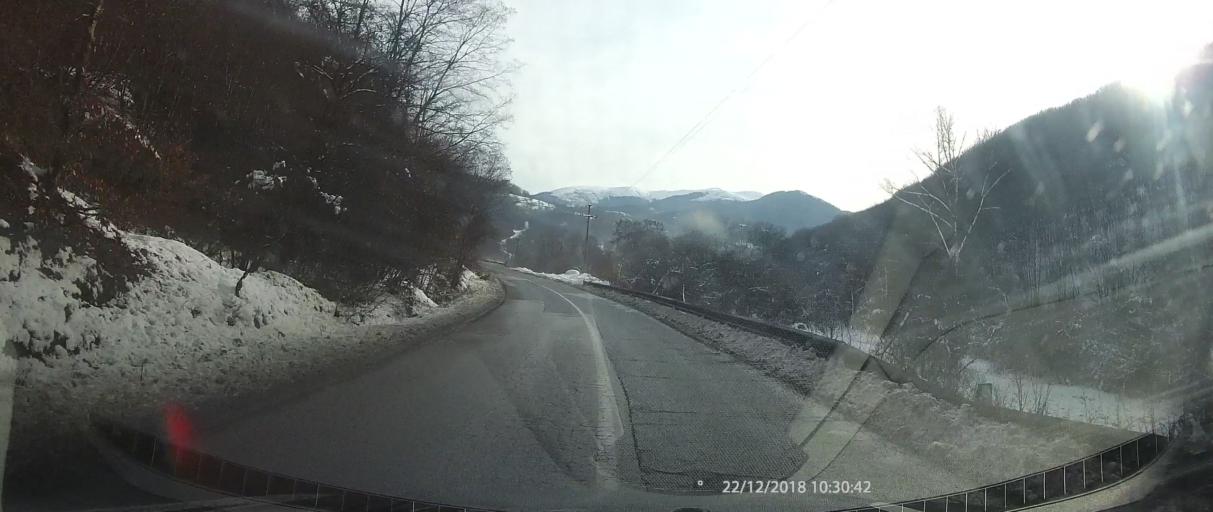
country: MK
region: Kriva Palanka
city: Kriva Palanka
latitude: 42.2249
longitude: 22.4144
